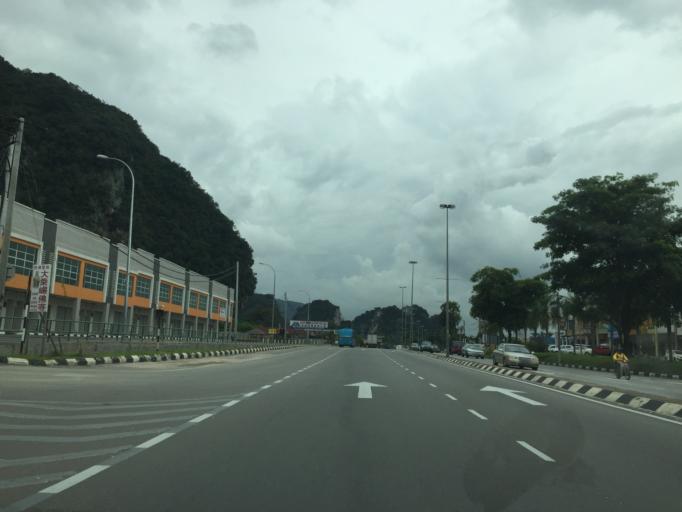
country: MY
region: Perak
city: Ipoh
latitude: 4.5558
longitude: 101.1147
